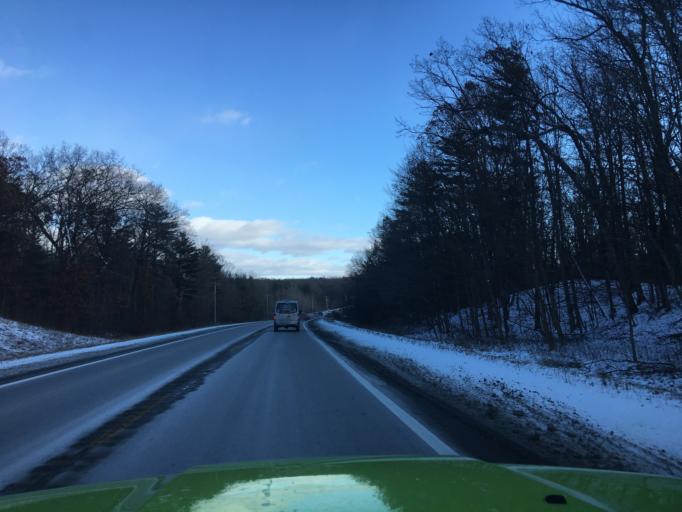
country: US
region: Michigan
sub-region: Kent County
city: Cedar Springs
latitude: 43.1787
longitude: -85.5476
